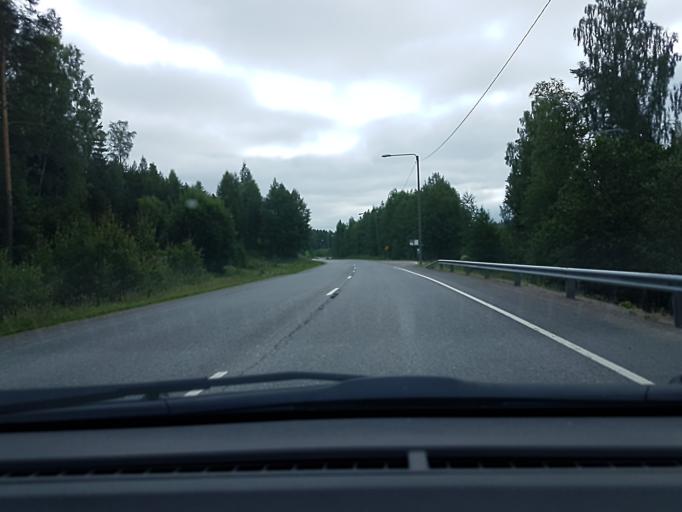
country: FI
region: Uusimaa
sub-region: Helsinki
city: Sibbo
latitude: 60.3603
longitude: 25.1947
